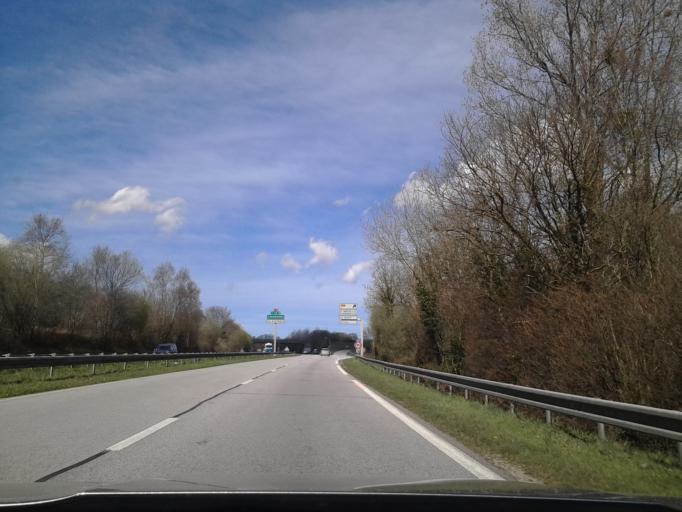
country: FR
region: Lower Normandy
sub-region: Departement de la Manche
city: Brix
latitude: 49.5609
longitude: -1.5672
